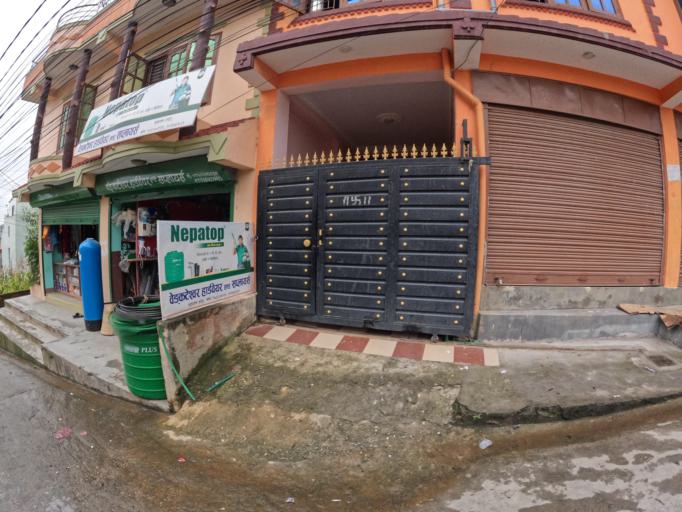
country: NP
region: Central Region
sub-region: Bagmati Zone
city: Kathmandu
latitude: 27.7583
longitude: 85.3227
